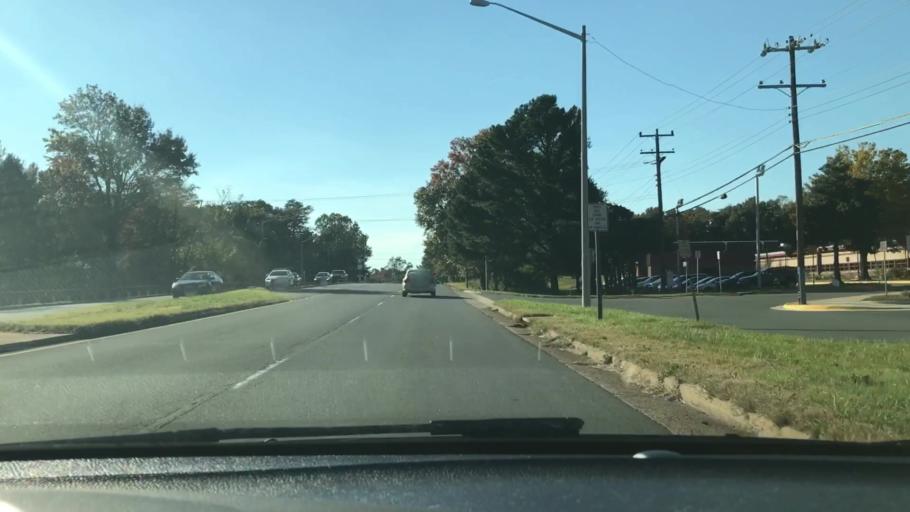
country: US
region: Virginia
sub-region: Fairfax County
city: Lake Barcroft
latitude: 38.8379
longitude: -77.1677
